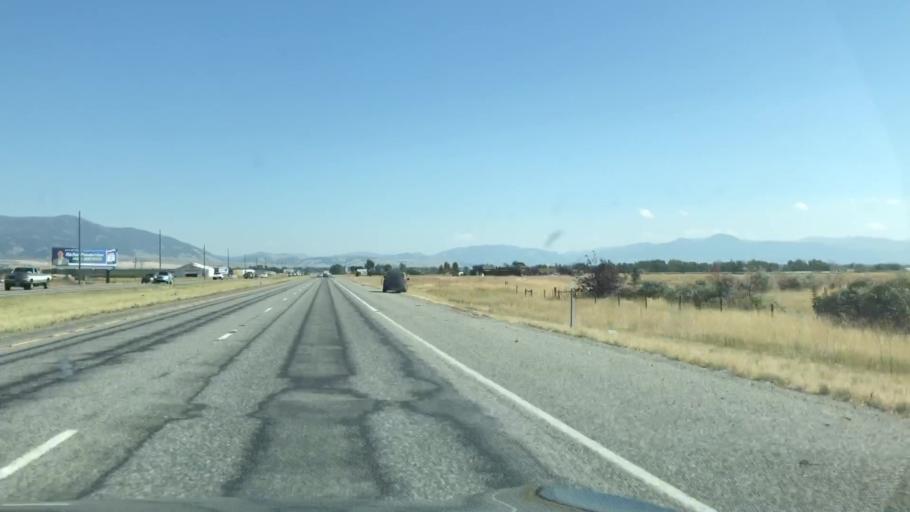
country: US
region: Montana
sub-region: Gallatin County
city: Belgrade
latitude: 45.7560
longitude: -111.1504
